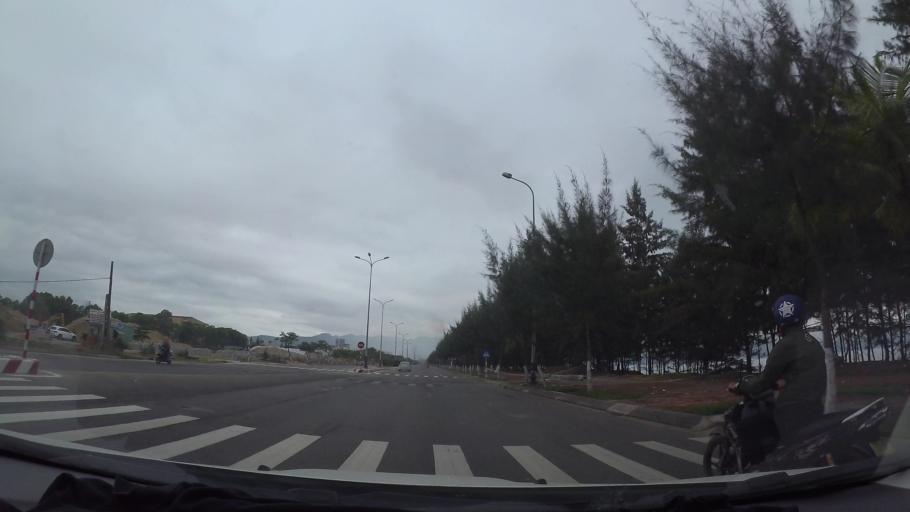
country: VN
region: Da Nang
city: Lien Chieu
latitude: 16.1022
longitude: 108.1392
